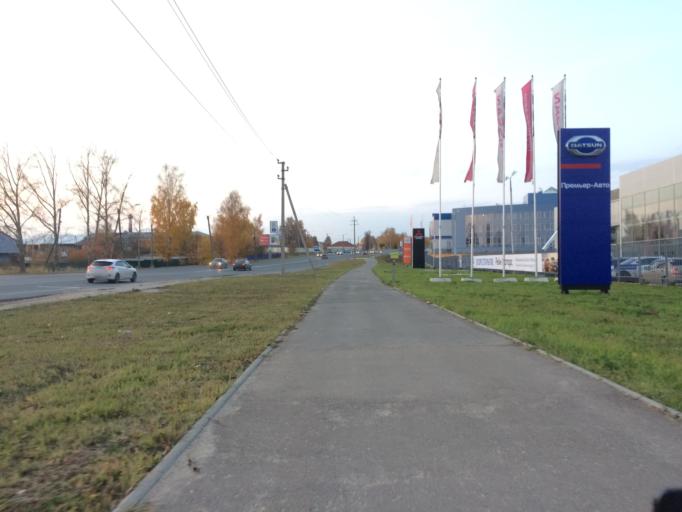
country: RU
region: Mariy-El
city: Yoshkar-Ola
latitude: 56.6041
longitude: 47.8819
